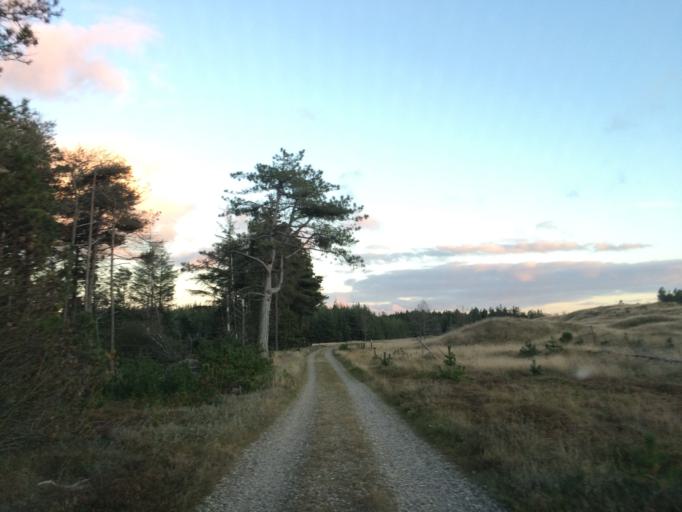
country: DK
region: Central Jutland
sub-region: Holstebro Kommune
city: Ulfborg
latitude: 56.2995
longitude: 8.1475
